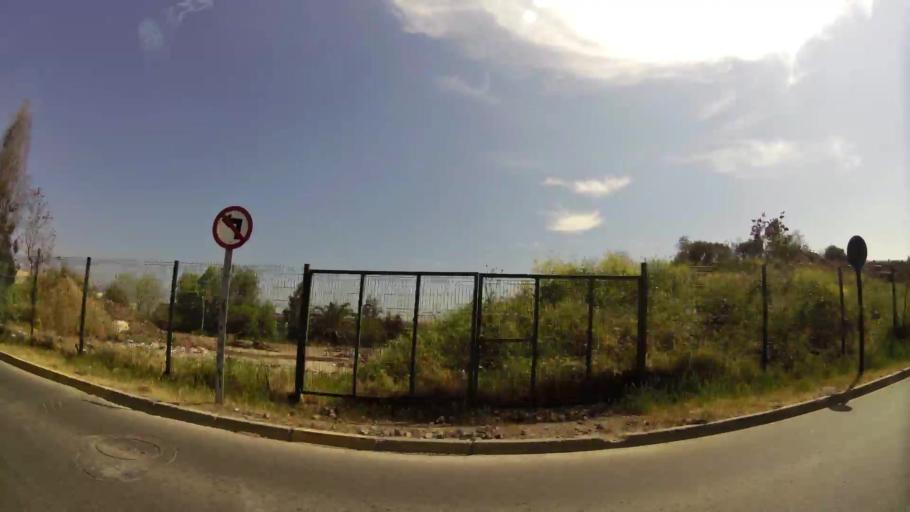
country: CL
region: Santiago Metropolitan
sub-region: Provincia de Santiago
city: Villa Presidente Frei, Nunoa, Santiago, Chile
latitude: -33.4659
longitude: -70.5493
